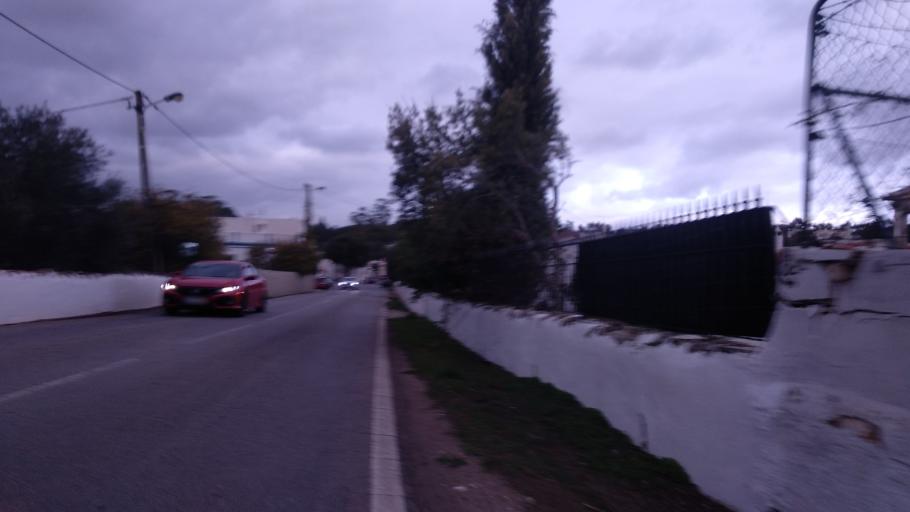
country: PT
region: Faro
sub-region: Sao Bras de Alportel
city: Sao Bras de Alportel
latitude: 37.1738
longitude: -7.9090
